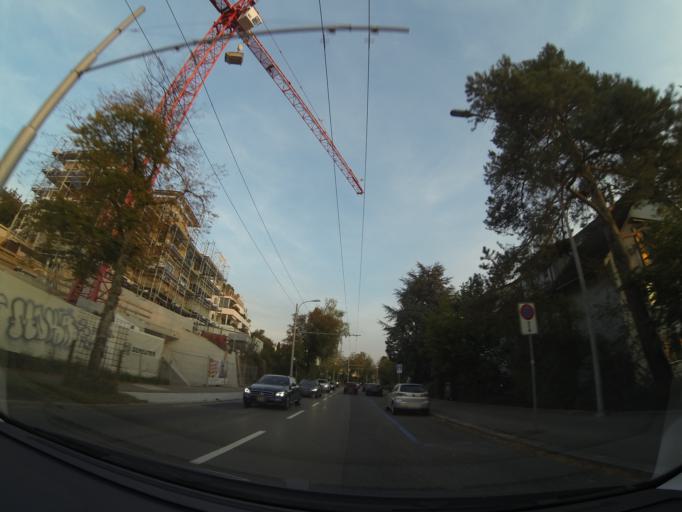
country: CH
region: Zurich
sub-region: Bezirk Zuerich
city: Zuerich (Kreis 10) / Ruetihof
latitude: 47.4119
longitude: 8.4844
